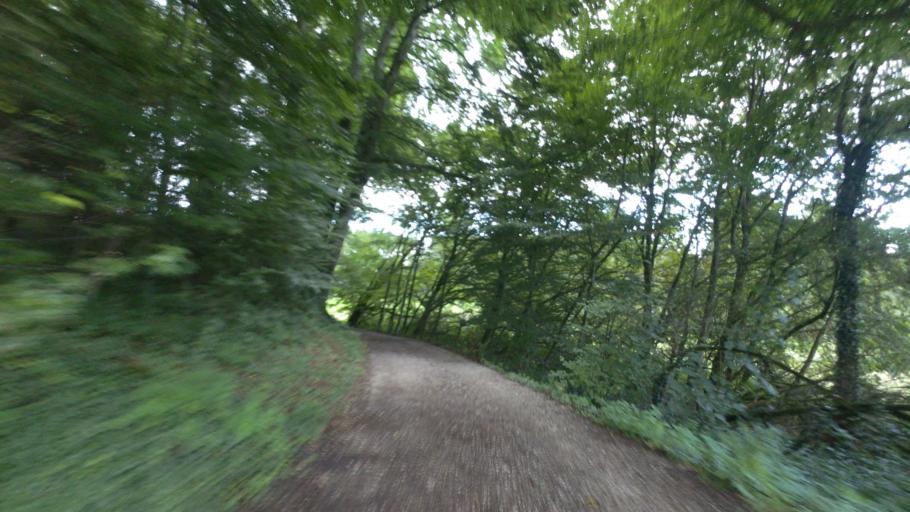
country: DE
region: Bavaria
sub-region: Upper Bavaria
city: Nussdorf
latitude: 47.9046
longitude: 12.5738
